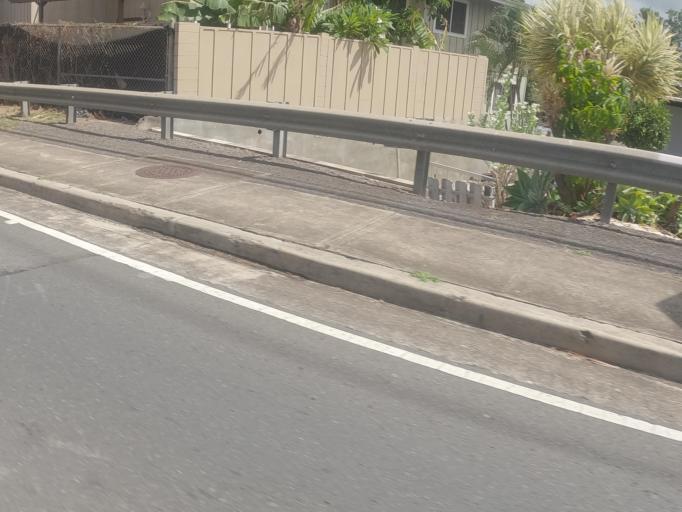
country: US
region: Hawaii
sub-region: Honolulu County
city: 'Aiea
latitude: 21.3768
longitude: -157.9337
